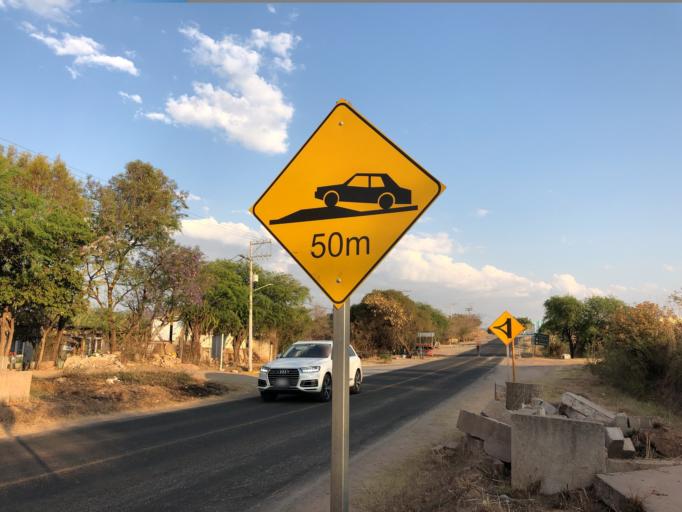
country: MX
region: Oaxaca
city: Ciudad de Huajuapam de Leon
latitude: 17.8364
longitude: -97.7908
